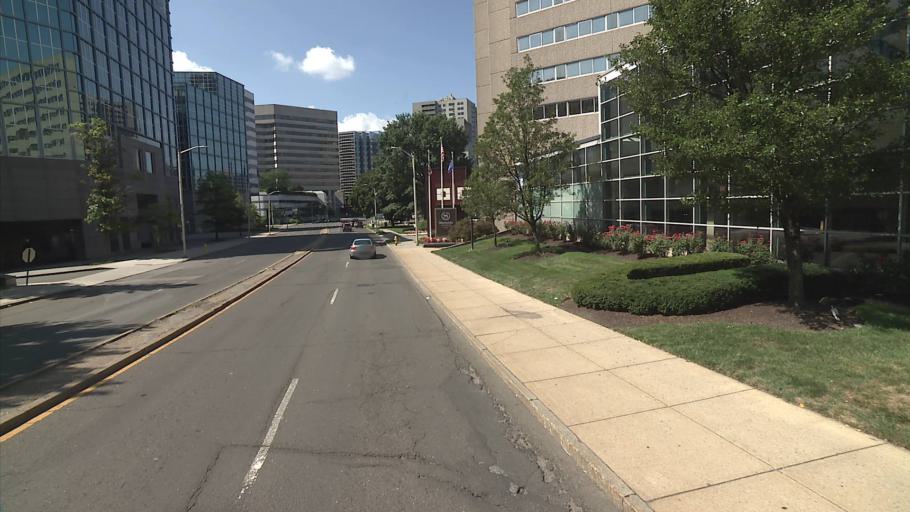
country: US
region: Connecticut
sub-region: Fairfield County
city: Stamford
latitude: 41.0547
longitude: -73.5318
